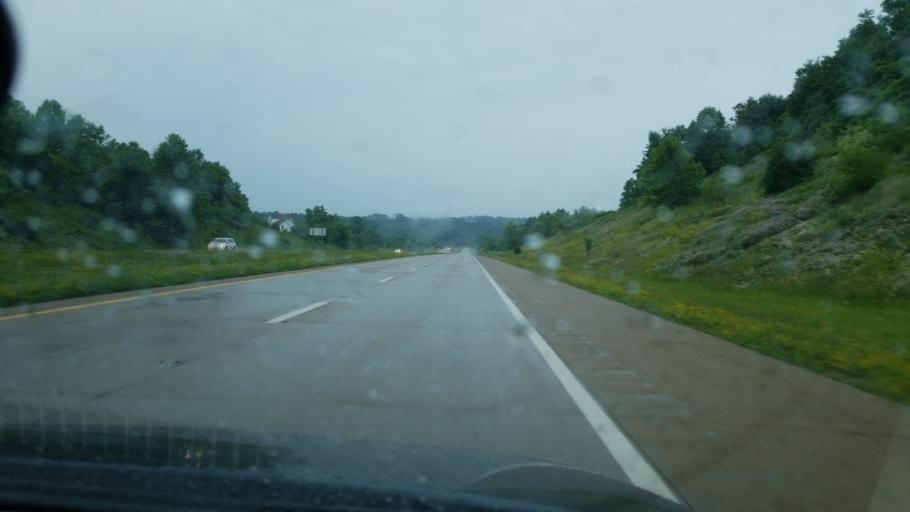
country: US
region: Ohio
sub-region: Athens County
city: Athens
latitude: 39.2573
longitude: -81.9087
